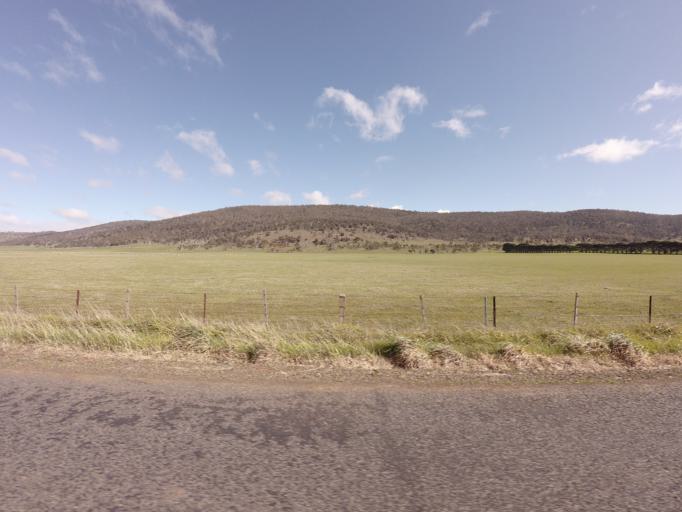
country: AU
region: Tasmania
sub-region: Northern Midlands
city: Evandale
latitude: -41.9685
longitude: 147.4420
